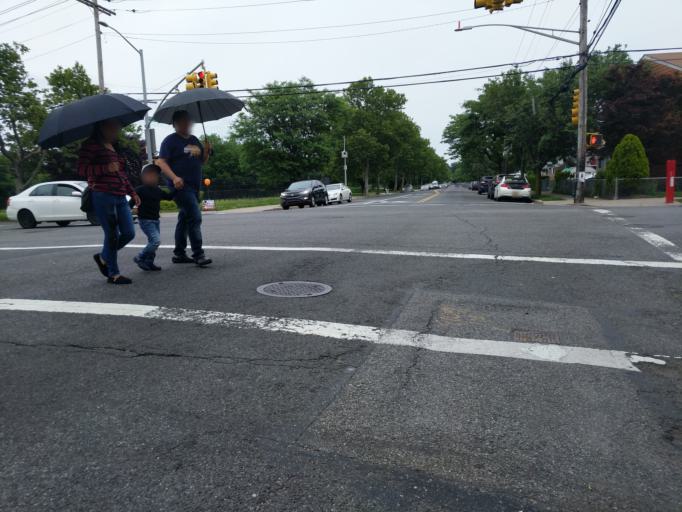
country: US
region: New York
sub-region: Queens County
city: Jamaica
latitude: 40.7430
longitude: -73.8145
